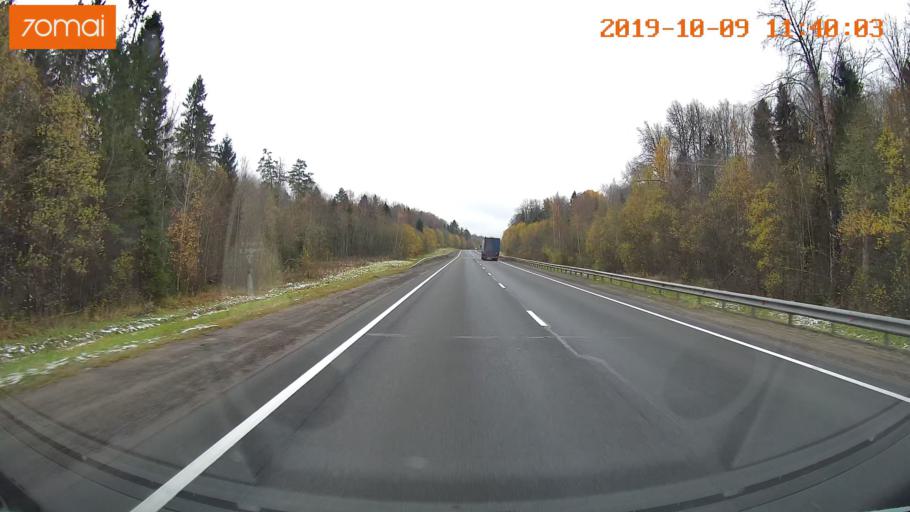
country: RU
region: Vologda
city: Gryazovets
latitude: 58.9483
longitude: 40.1720
